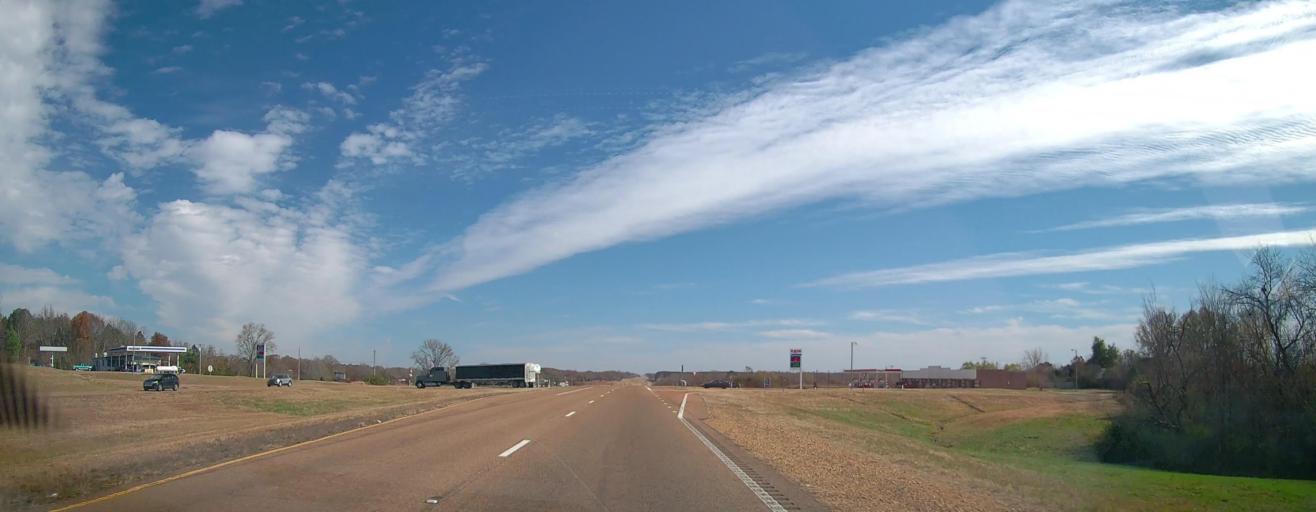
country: US
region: Mississippi
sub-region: Marshall County
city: Holly Springs
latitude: 34.9462
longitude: -89.3895
